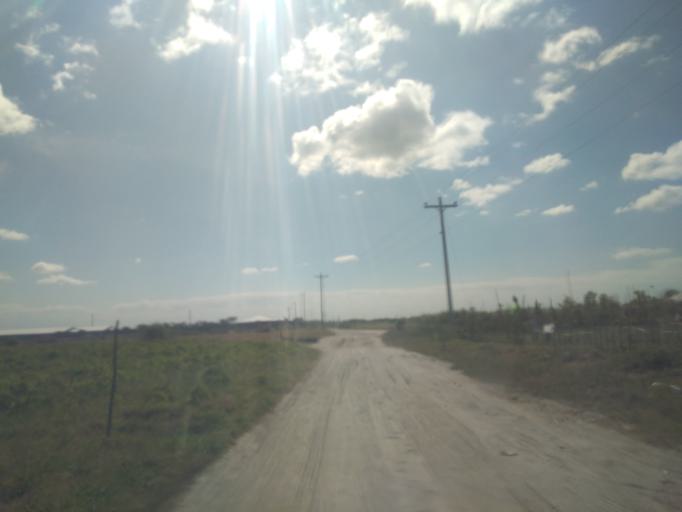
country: PH
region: Central Luzon
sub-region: Province of Pampanga
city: Balas
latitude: 15.0650
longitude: 120.5923
